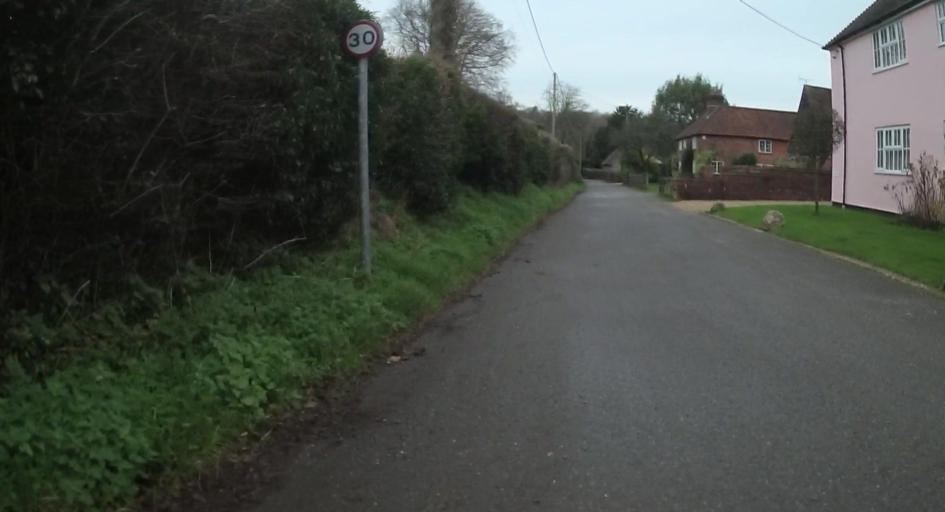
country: GB
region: England
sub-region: Hampshire
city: Alton
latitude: 51.1126
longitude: -0.9813
